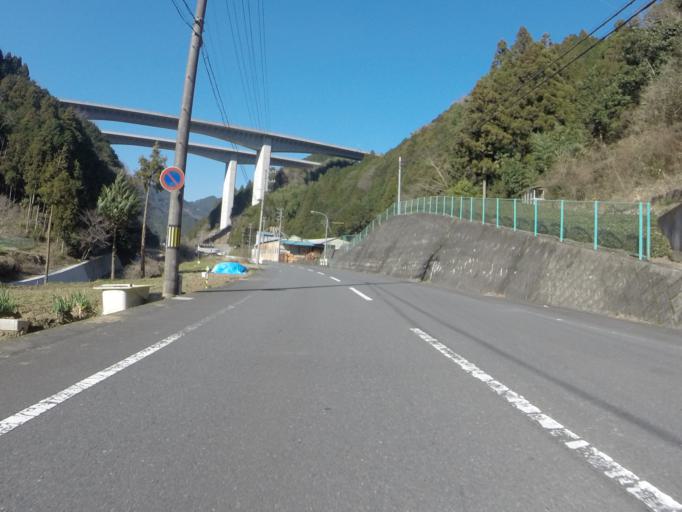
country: JP
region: Shizuoka
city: Fujinomiya
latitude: 35.1119
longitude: 138.4891
